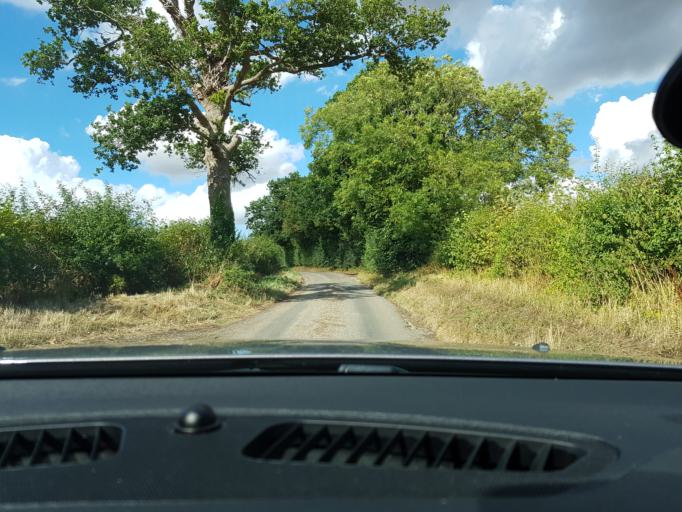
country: GB
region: England
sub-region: Wiltshire
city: Ramsbury
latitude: 51.4473
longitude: -1.5791
